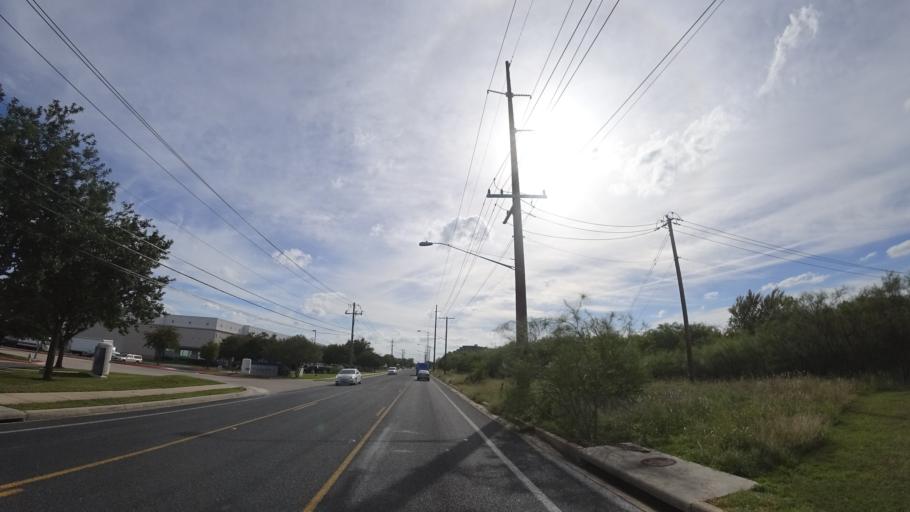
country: US
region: Texas
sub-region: Travis County
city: Austin
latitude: 30.2065
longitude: -97.7519
